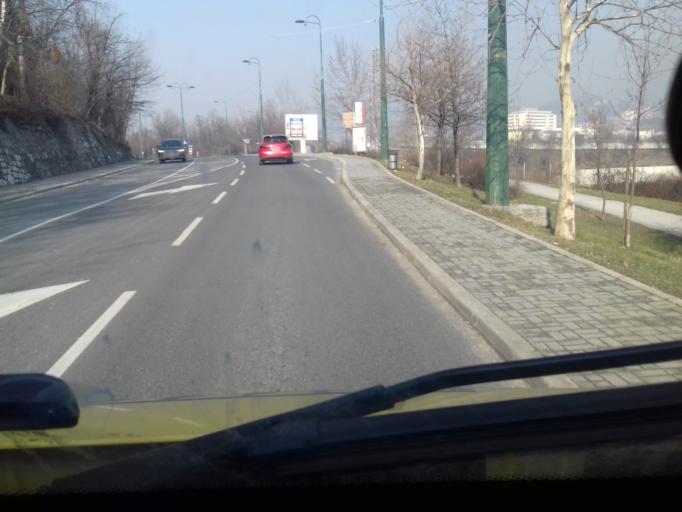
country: BA
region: Federation of Bosnia and Herzegovina
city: Kobilja Glava
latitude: 43.8707
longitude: 18.4076
